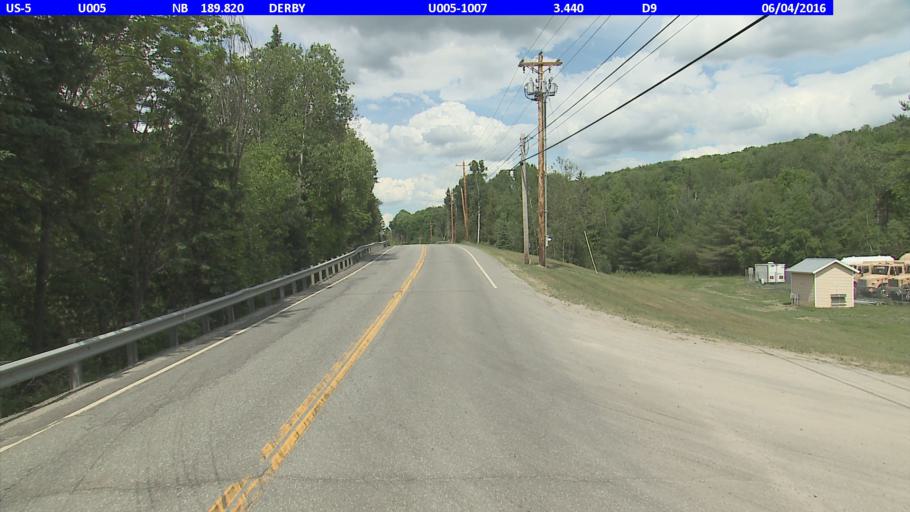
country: US
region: Vermont
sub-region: Orleans County
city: Newport
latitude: 44.9730
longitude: -72.1180
